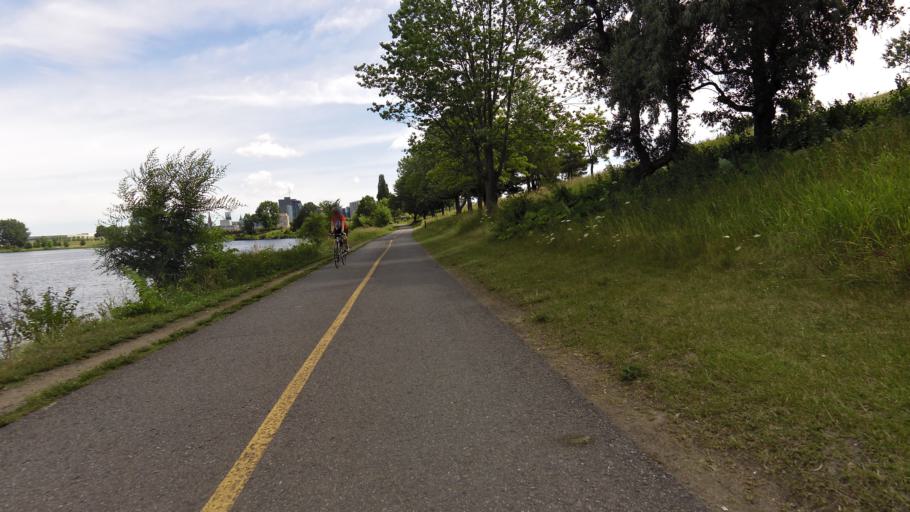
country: CA
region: Ontario
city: Ottawa
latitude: 45.4119
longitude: -75.7235
